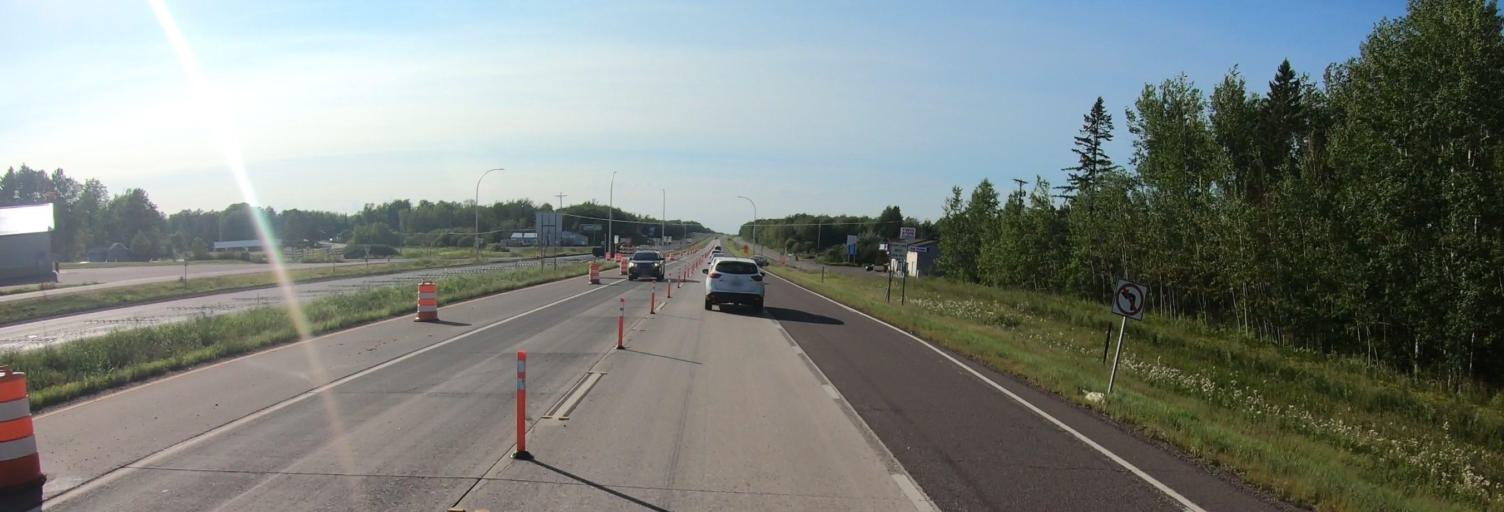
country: US
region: Minnesota
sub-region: Saint Louis County
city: Hermantown
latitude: 46.8937
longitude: -92.3630
